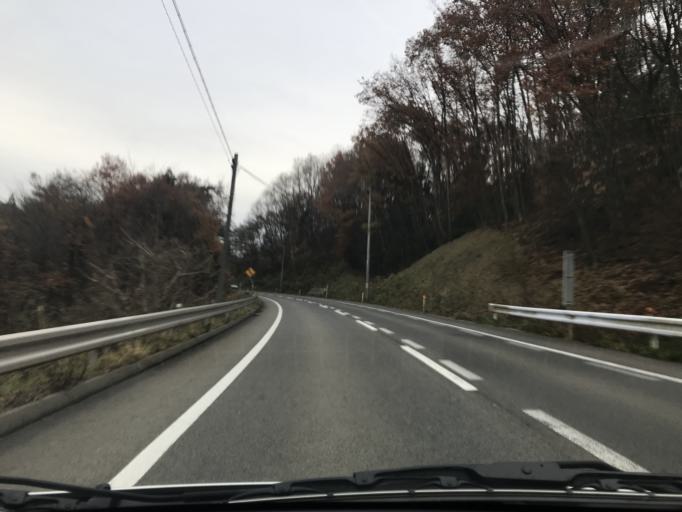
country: JP
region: Iwate
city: Kitakami
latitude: 39.2841
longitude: 141.2311
